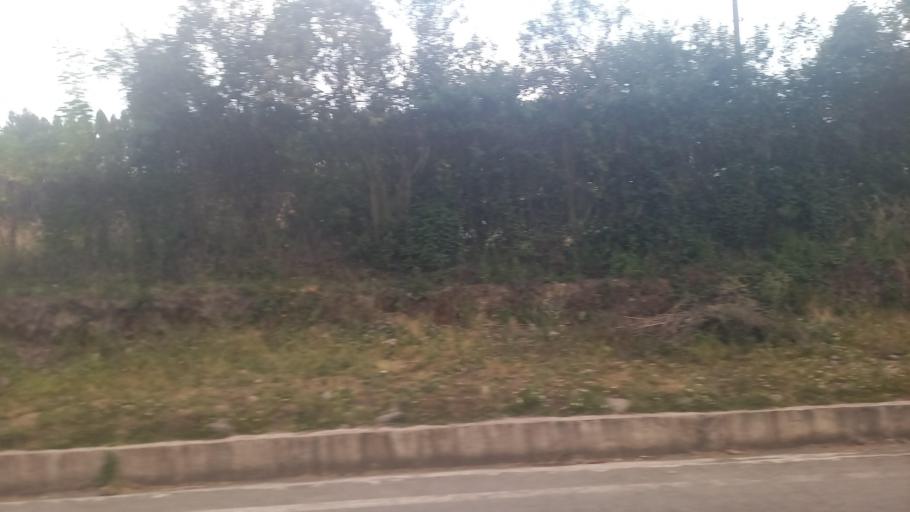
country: EC
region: Pichincha
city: Cayambe
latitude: 0.0912
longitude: -78.0973
